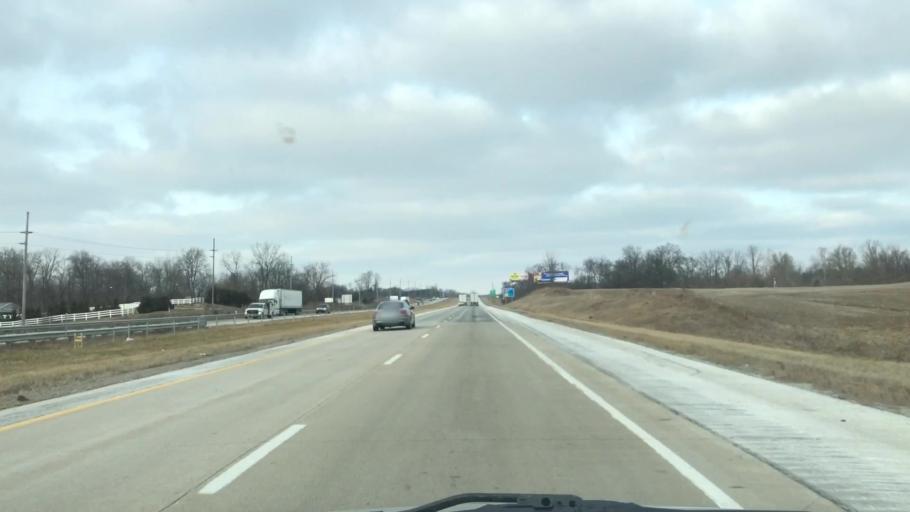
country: US
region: Indiana
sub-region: Steuben County
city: Angola
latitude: 41.6099
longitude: -85.0469
